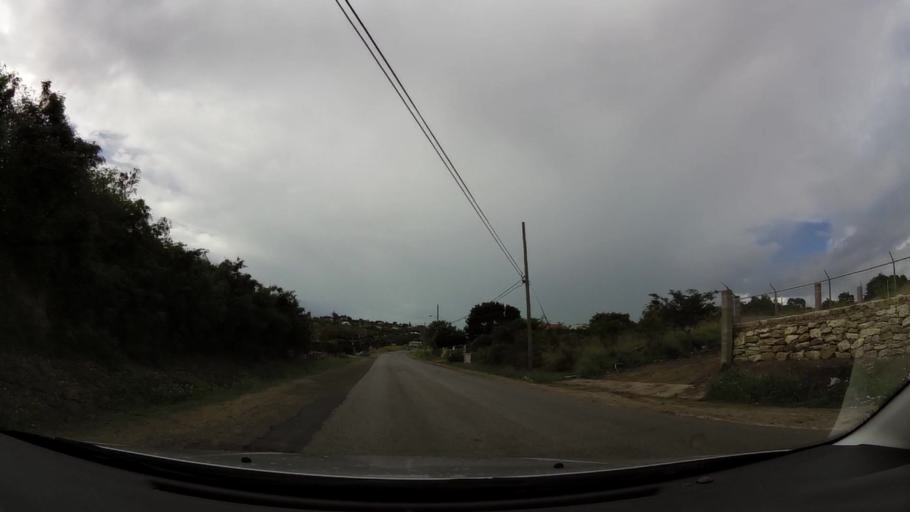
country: AG
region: Saint John
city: Potters Village
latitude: 17.0903
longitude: -61.8152
